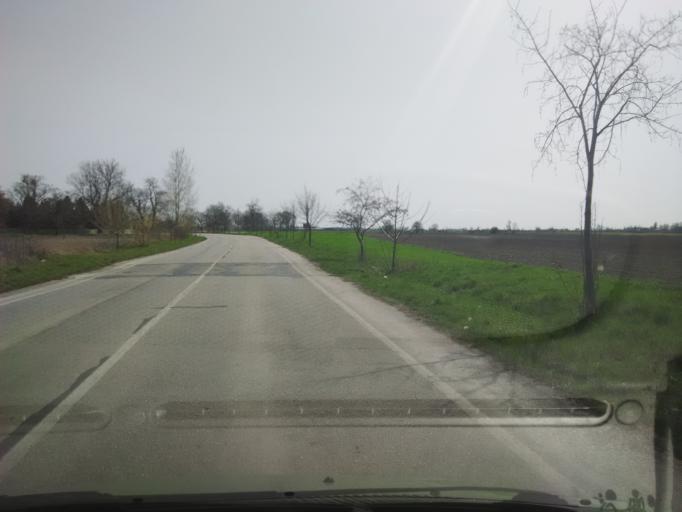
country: SK
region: Bratislavsky
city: Senec
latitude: 48.1182
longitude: 17.4343
